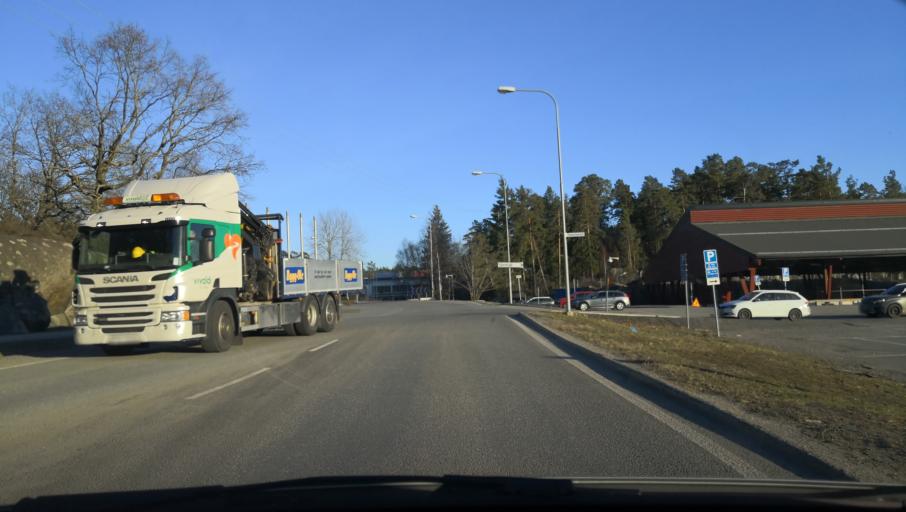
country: SE
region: Stockholm
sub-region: Varmdo Kommun
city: Gustavsberg
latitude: 59.3282
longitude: 18.3947
